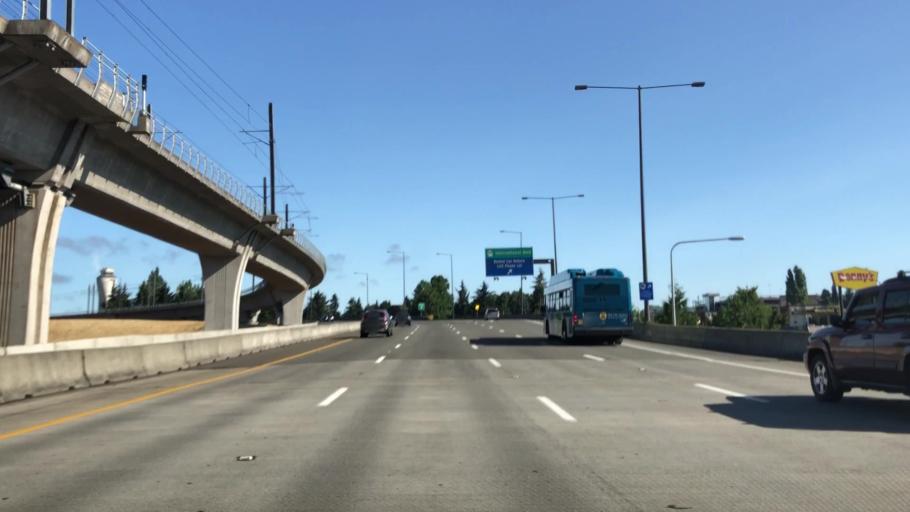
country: US
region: Washington
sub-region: King County
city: SeaTac
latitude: 47.4469
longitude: -122.2982
